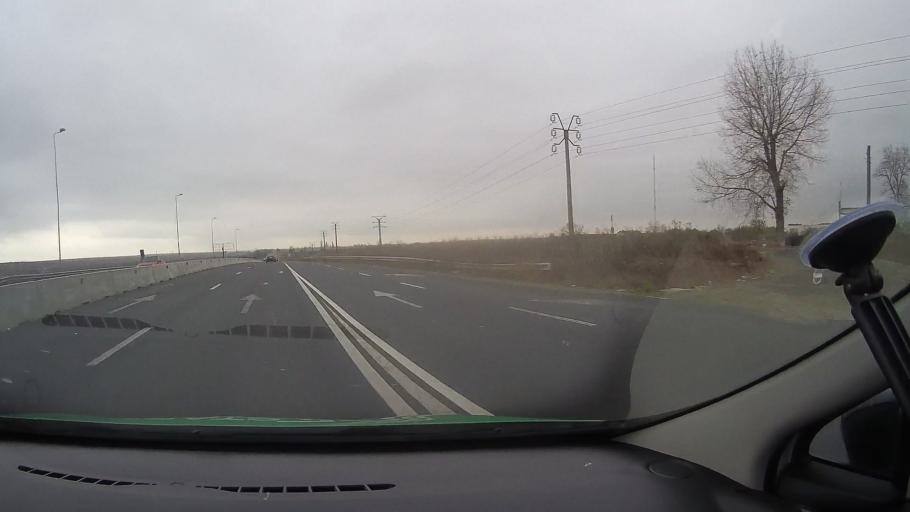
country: RO
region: Constanta
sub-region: Comuna Cumpana
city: Cumpana
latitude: 44.1666
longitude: 28.5436
